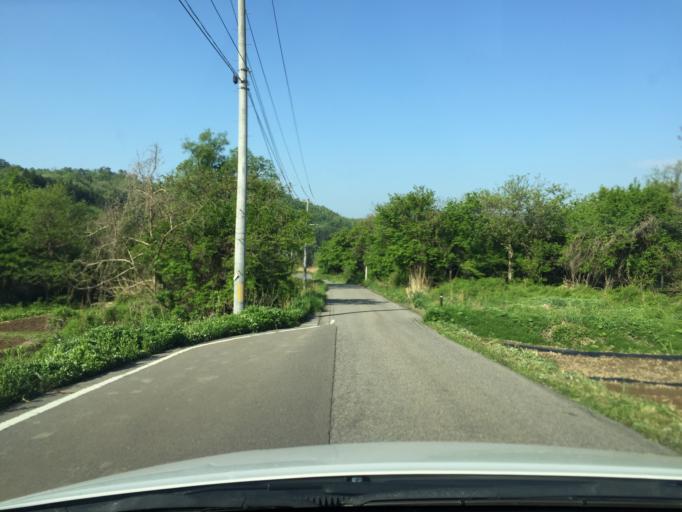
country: JP
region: Fukushima
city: Kitakata
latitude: 37.6768
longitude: 139.8000
